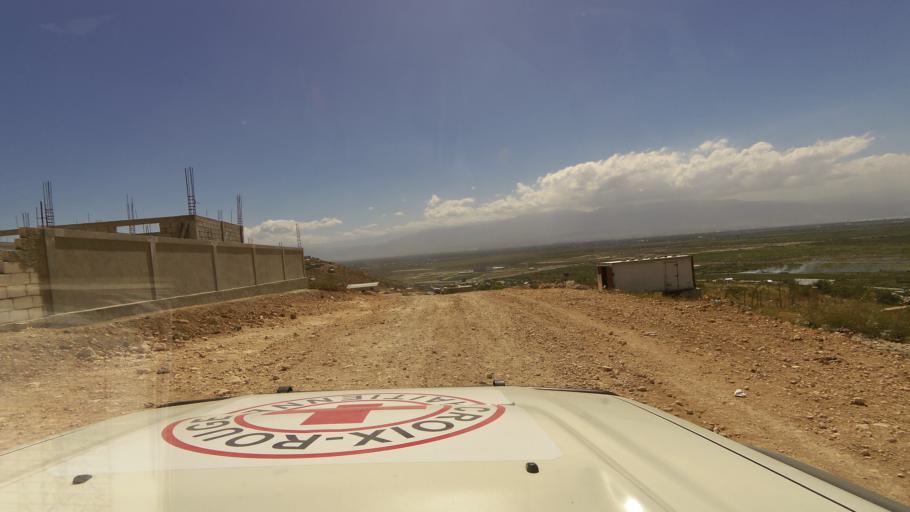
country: HT
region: Ouest
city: Croix des Bouquets
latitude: 18.6687
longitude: -72.2936
